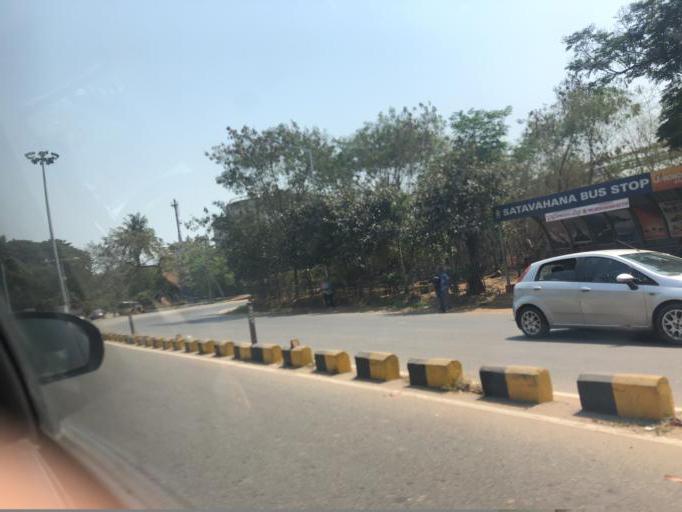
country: IN
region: Andhra Pradesh
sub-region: Vishakhapatnam
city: Yarada
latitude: 17.6979
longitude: 83.2690
